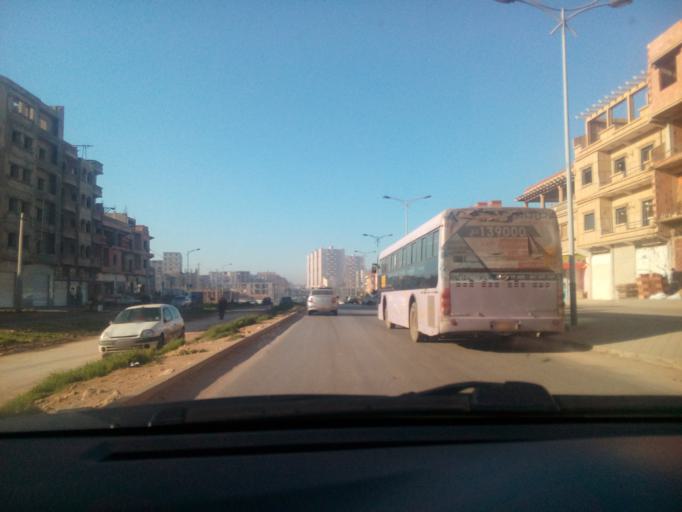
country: DZ
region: Oran
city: Bir el Djir
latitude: 35.7523
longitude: -0.5486
